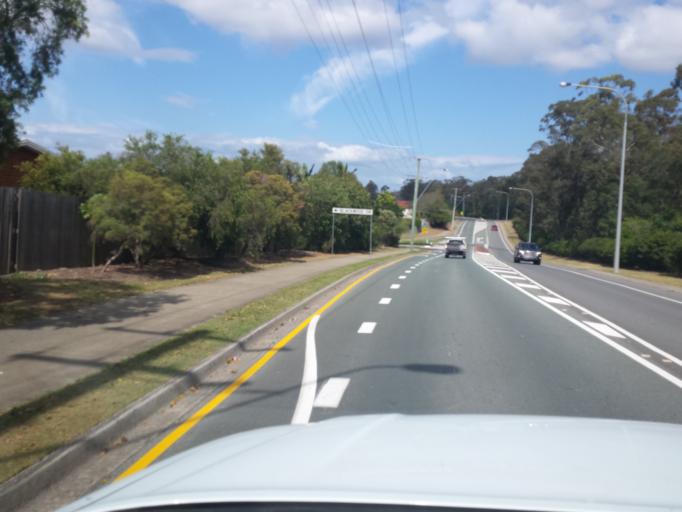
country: AU
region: Queensland
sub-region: Moreton Bay
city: Ferny Hills
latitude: -27.3817
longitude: 152.9466
